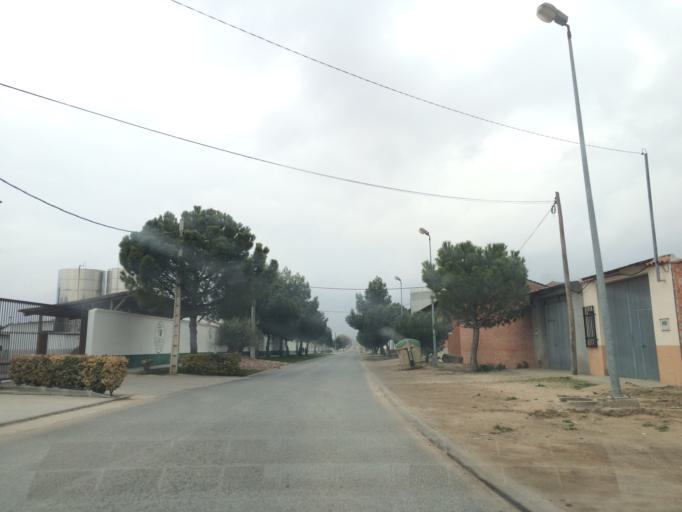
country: ES
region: Castille-La Mancha
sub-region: Province of Toledo
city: Madridejos
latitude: 39.4736
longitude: -3.5303
